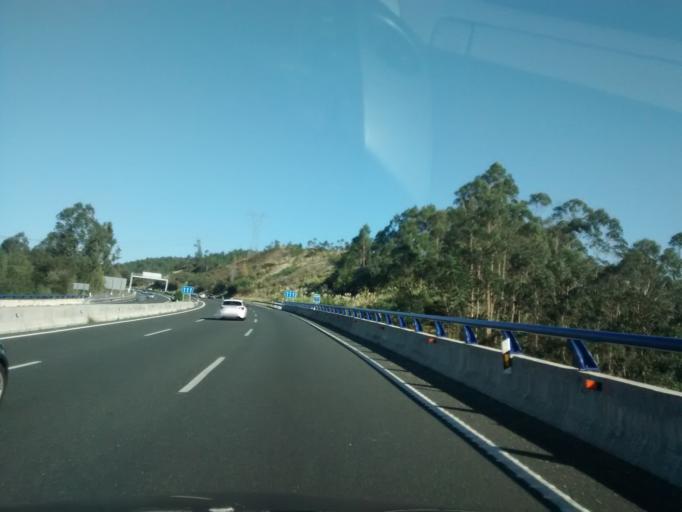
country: ES
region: Cantabria
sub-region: Provincia de Cantabria
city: Luzmela
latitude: 43.3229
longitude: -4.1813
